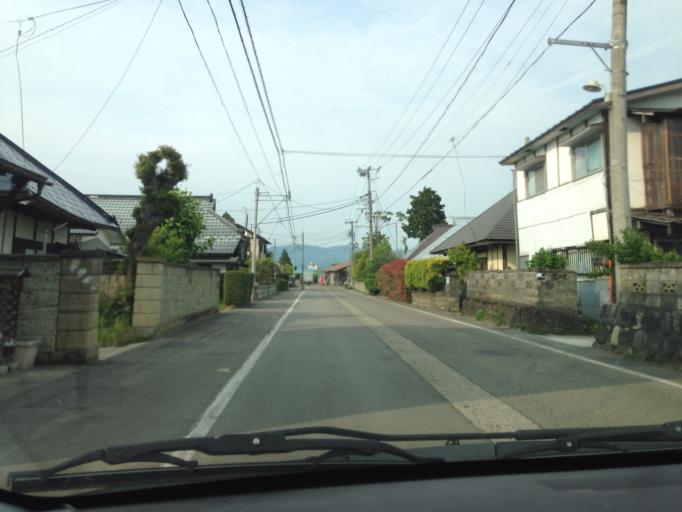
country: JP
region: Fukushima
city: Kitakata
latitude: 37.4580
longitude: 139.8933
